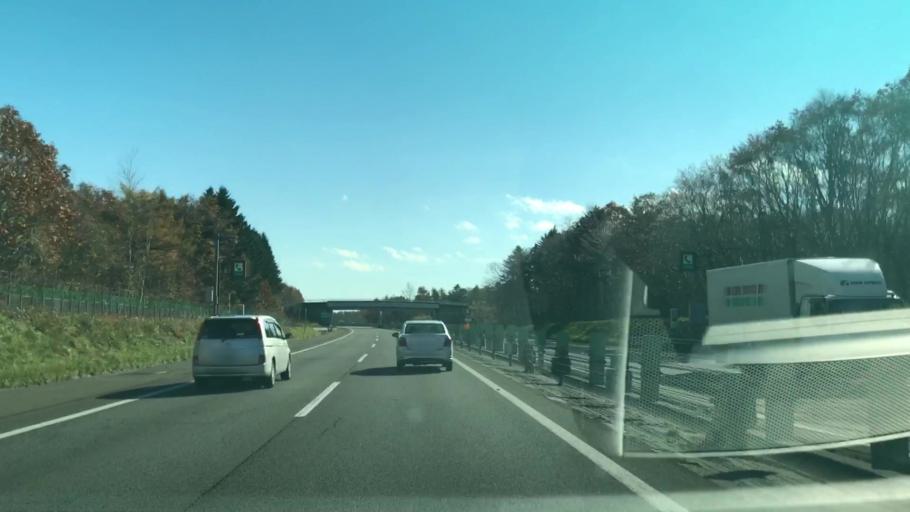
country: JP
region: Hokkaido
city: Chitose
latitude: 42.8589
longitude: 141.5607
